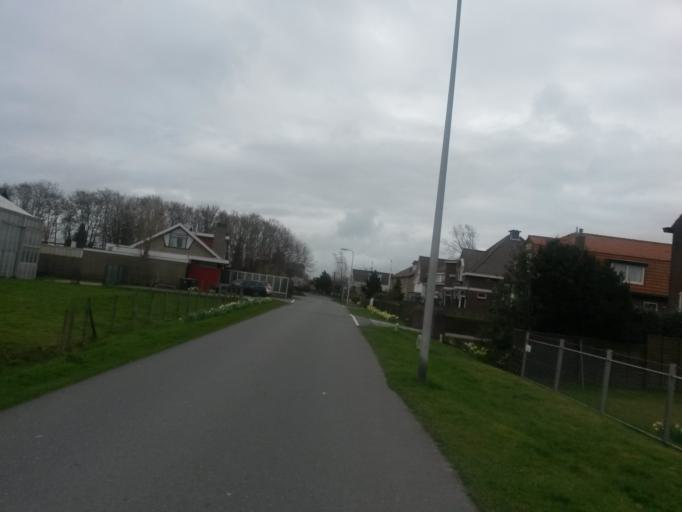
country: NL
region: South Holland
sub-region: Gemeente Rotterdam
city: Hoek van Holland
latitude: 52.0005
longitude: 4.1404
